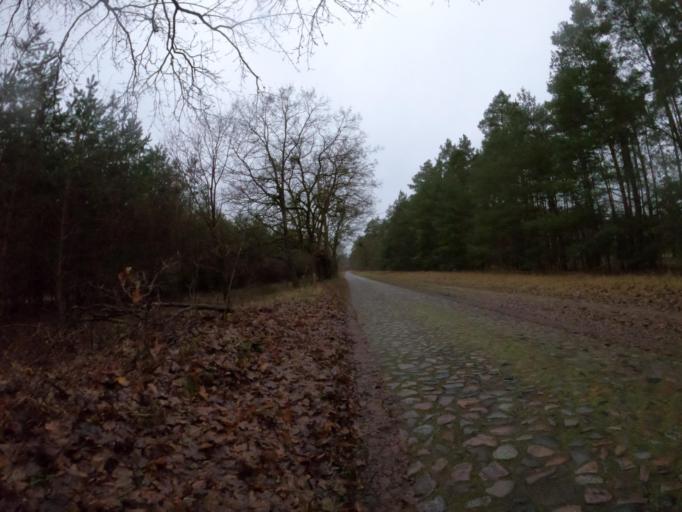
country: PL
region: West Pomeranian Voivodeship
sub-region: Powiat mysliborski
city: Debno
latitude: 52.8094
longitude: 14.7361
